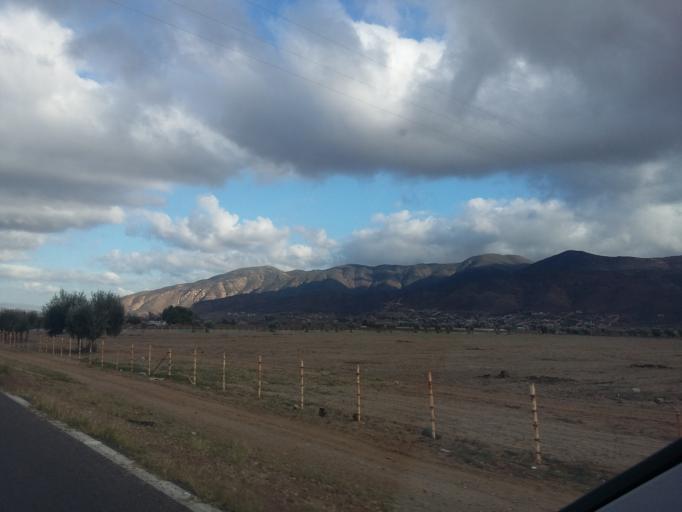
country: MX
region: Baja California
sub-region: Ensenada
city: Rancho Verde
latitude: 32.0866
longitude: -116.5959
